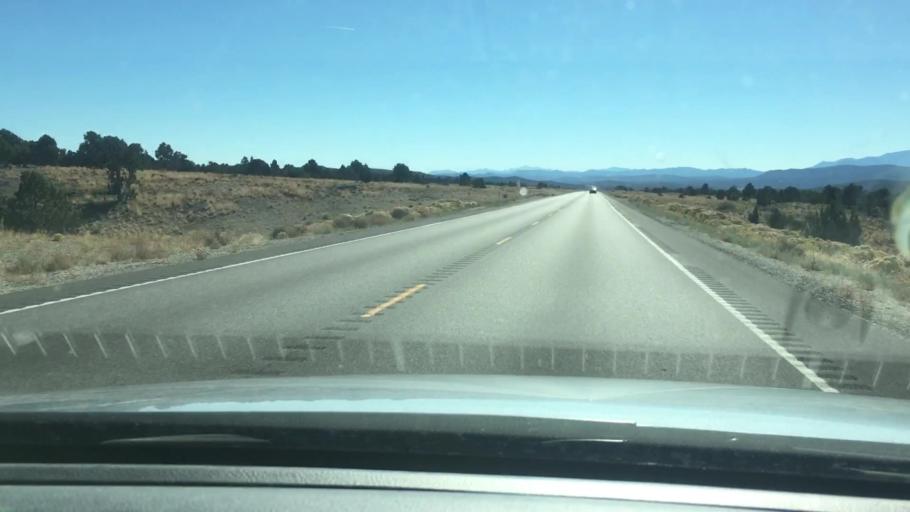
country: US
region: Nevada
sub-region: White Pine County
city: Ely
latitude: 39.1698
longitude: -115.0202
